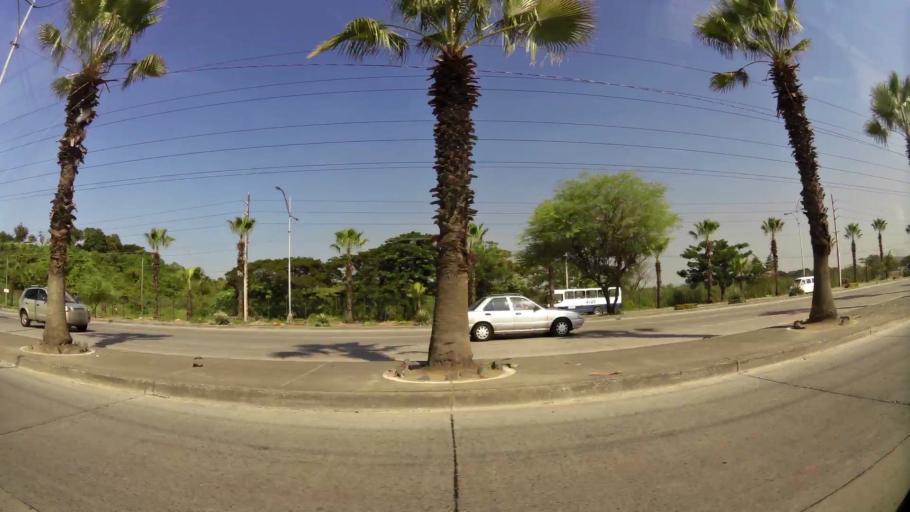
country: EC
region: Guayas
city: Eloy Alfaro
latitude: -2.1048
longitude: -79.9093
